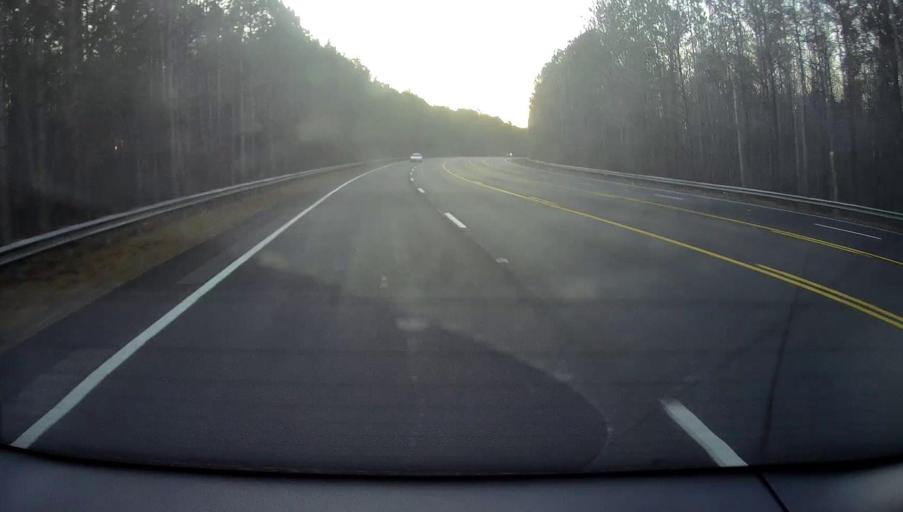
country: US
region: Georgia
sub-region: Fulton County
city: Union City
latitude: 33.5520
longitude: -84.4956
